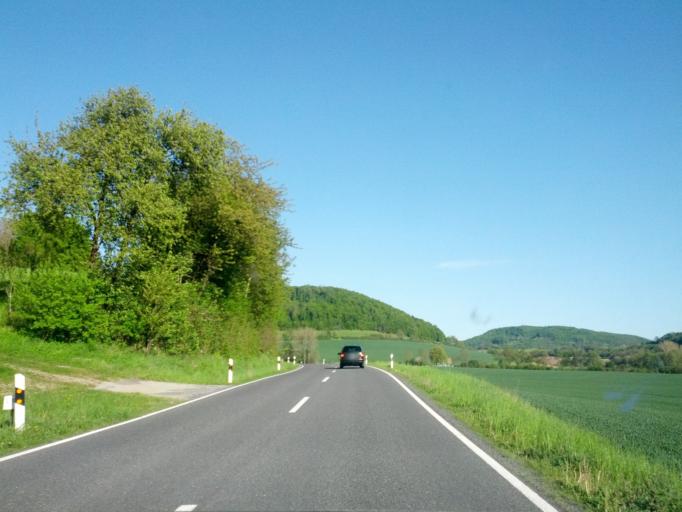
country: DE
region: Thuringia
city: Geismar
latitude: 51.2268
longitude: 10.1800
